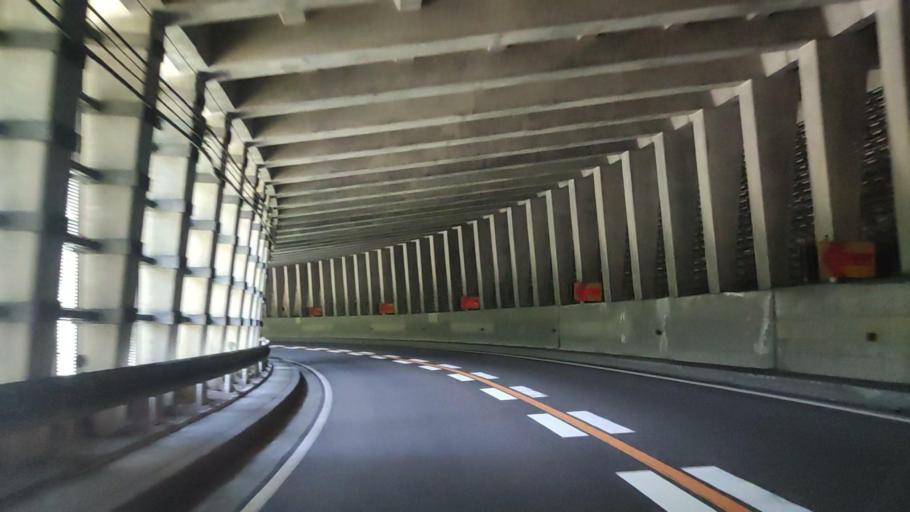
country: JP
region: Niigata
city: Itoigawa
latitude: 36.9078
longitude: 137.8615
